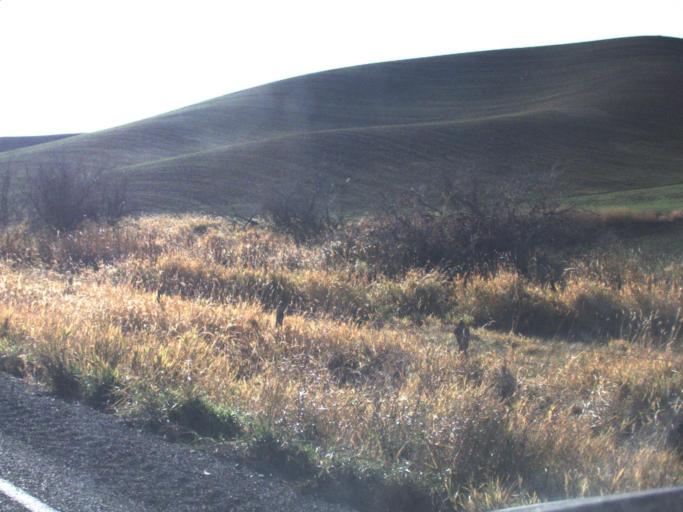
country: US
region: Washington
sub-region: Whitman County
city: Colfax
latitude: 46.7662
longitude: -117.3908
